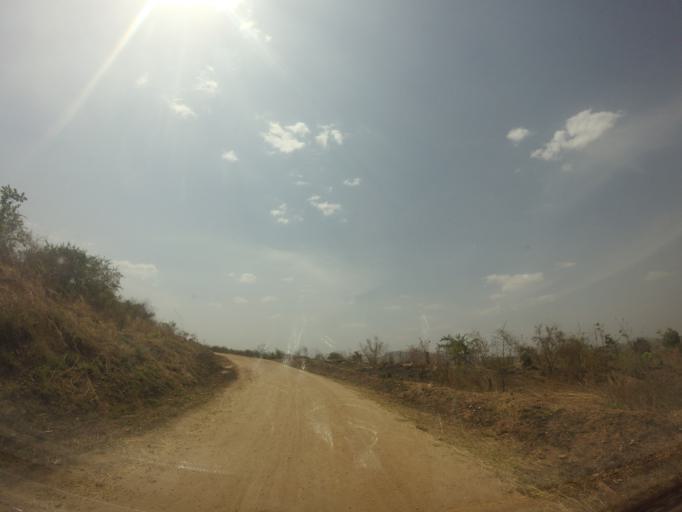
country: UG
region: Northern Region
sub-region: Arua District
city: Arua
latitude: 2.9090
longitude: 31.0621
